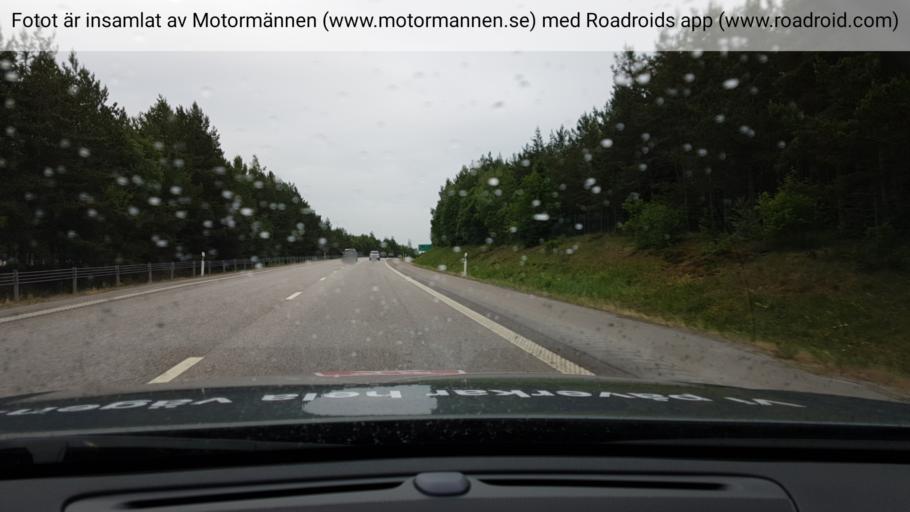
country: SE
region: Uppsala
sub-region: Knivsta Kommun
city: Knivsta
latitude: 59.7015
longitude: 17.8585
